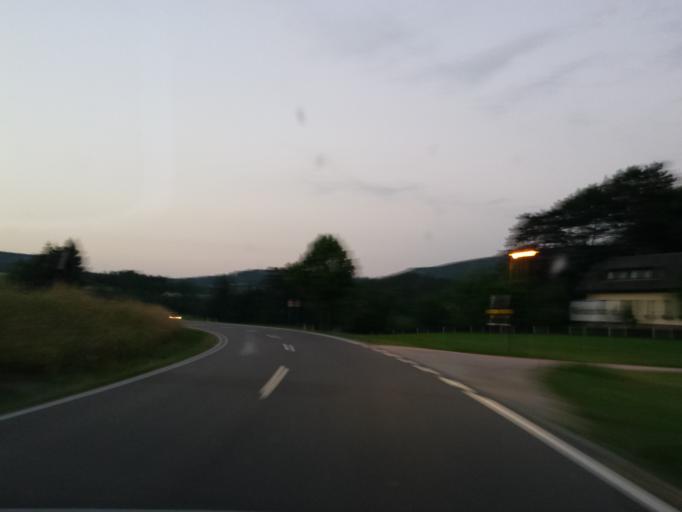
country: AT
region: Lower Austria
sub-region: Politischer Bezirk Baden
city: Altenmarkt an der Triesting
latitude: 48.0227
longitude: 16.0191
